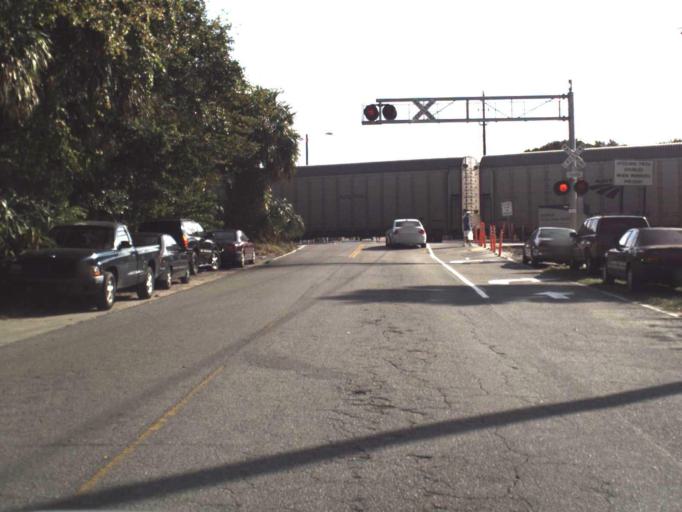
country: US
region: Florida
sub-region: Seminole County
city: Sanford
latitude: 28.8081
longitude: -81.2889
